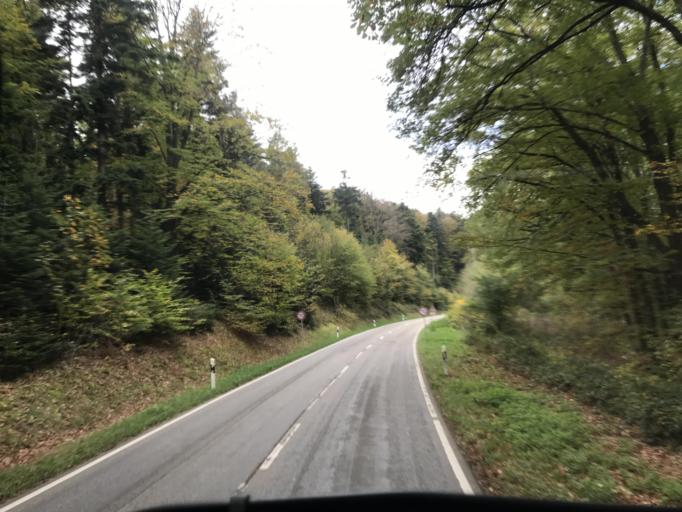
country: DE
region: Baden-Wuerttemberg
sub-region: Karlsruhe Region
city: Baden-Baden
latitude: 48.7747
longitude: 8.2838
